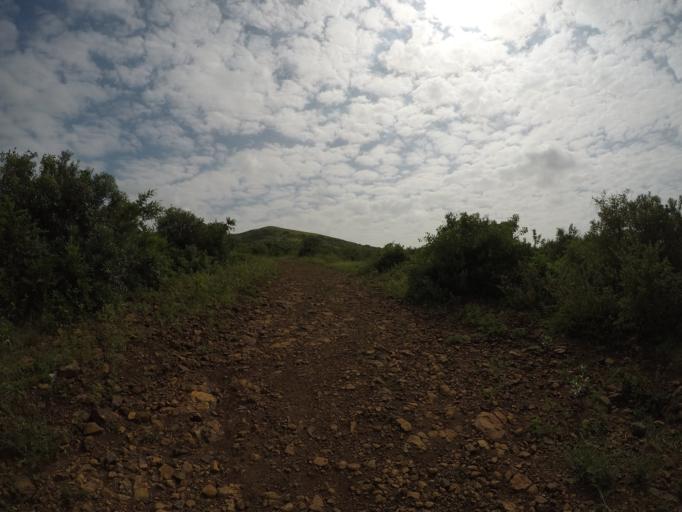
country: ZA
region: KwaZulu-Natal
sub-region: uThungulu District Municipality
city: Empangeni
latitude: -28.6137
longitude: 31.9047
